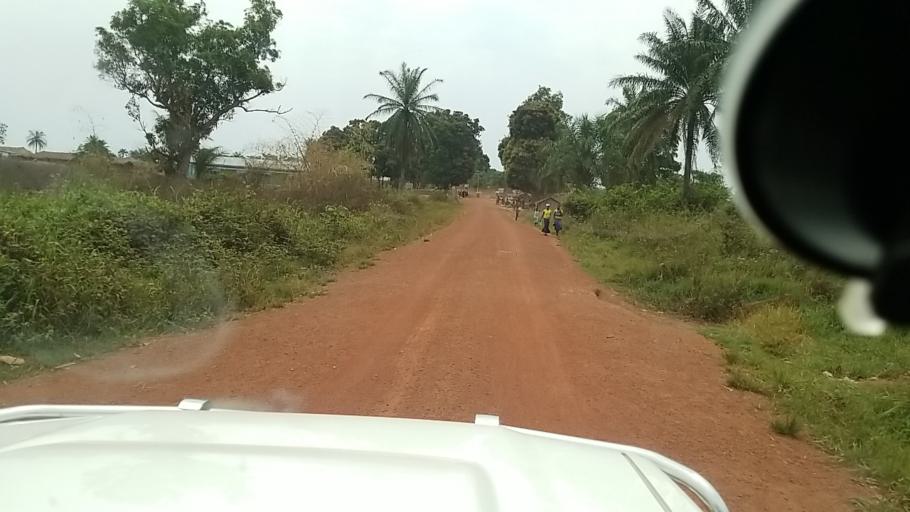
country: CD
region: Equateur
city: Libenge
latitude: 3.7295
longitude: 18.7733
